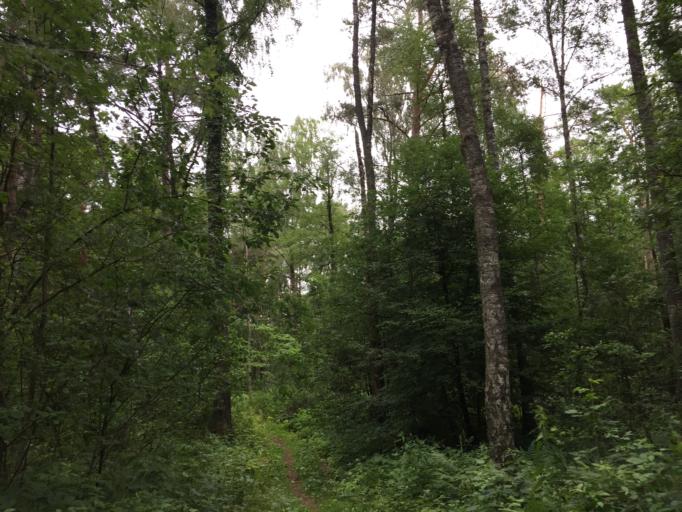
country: LV
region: Carnikava
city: Carnikava
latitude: 57.1188
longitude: 24.2220
